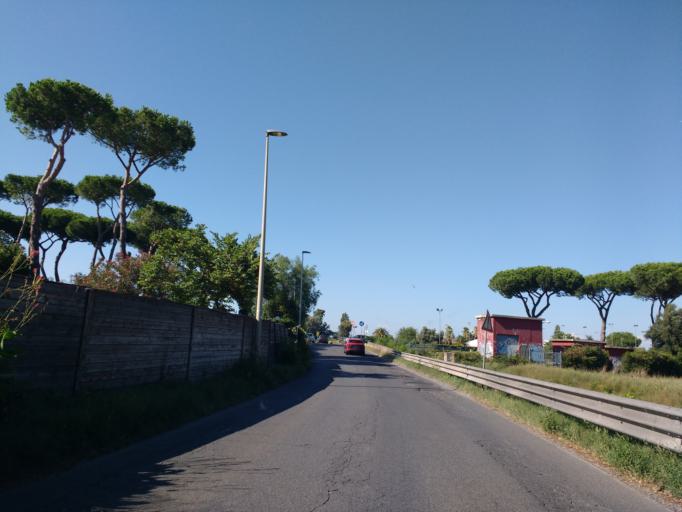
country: IT
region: Latium
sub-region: Citta metropolitana di Roma Capitale
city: Acilia-Castel Fusano-Ostia Antica
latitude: 41.7511
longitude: 12.3301
